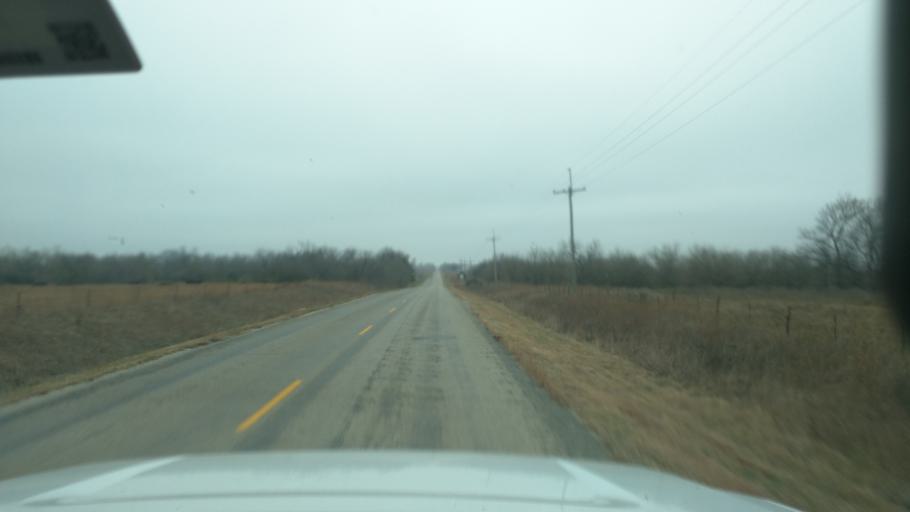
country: US
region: Kansas
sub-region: Lyon County
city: Emporia
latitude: 38.5978
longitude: -96.2609
